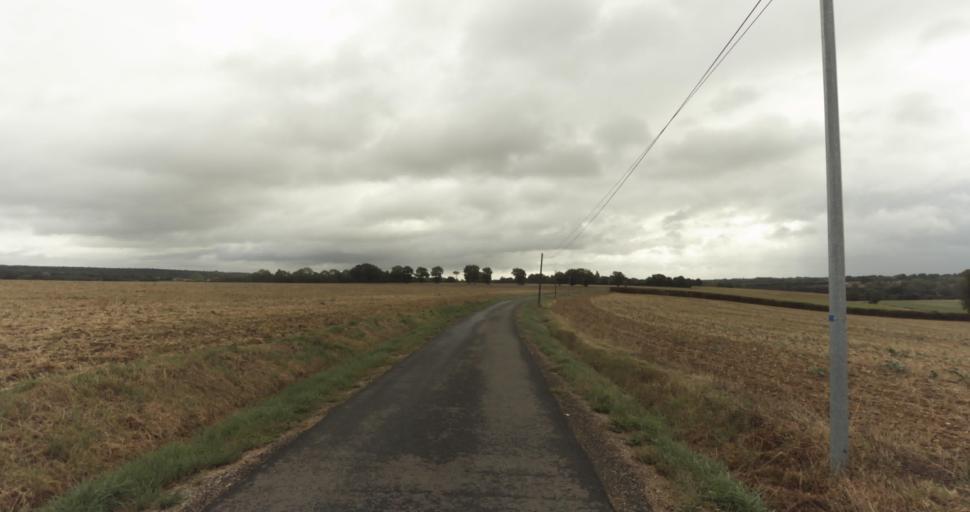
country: FR
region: Lower Normandy
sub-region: Departement de l'Orne
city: Sainte-Gauburge-Sainte-Colombe
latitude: 48.7341
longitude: 0.4499
